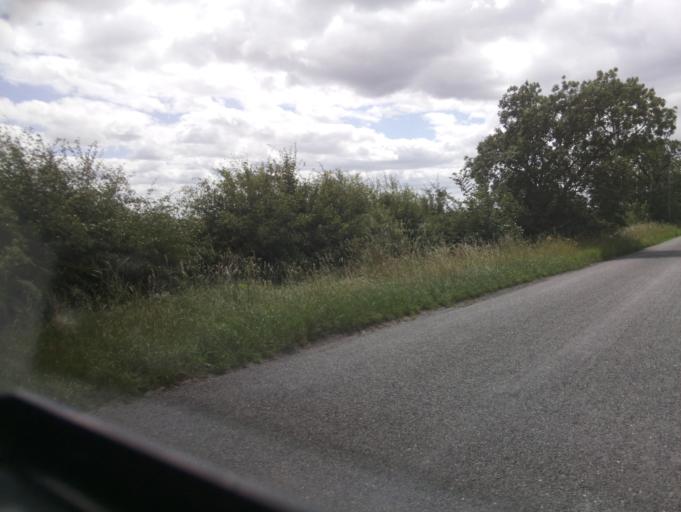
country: GB
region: England
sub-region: Nottinghamshire
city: Ruddington
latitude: 52.8651
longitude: -1.0941
